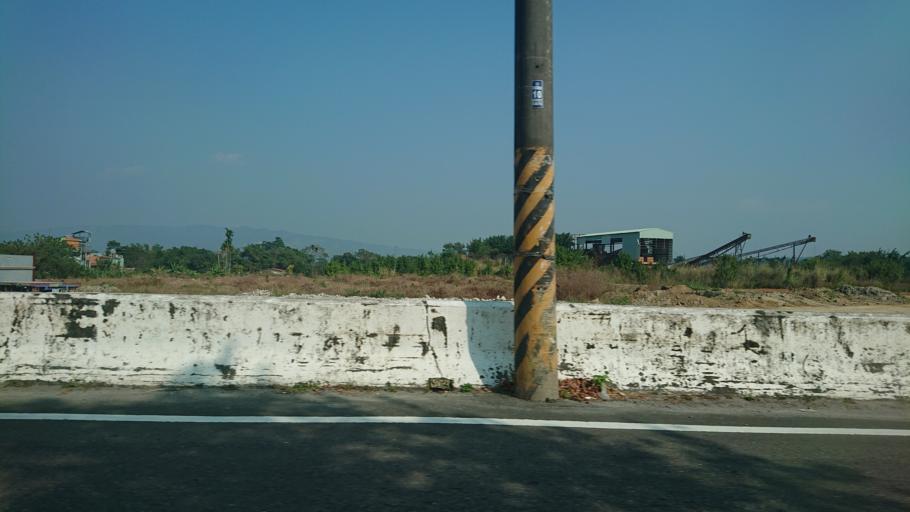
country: TW
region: Taiwan
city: Lugu
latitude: 23.7588
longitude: 120.6598
